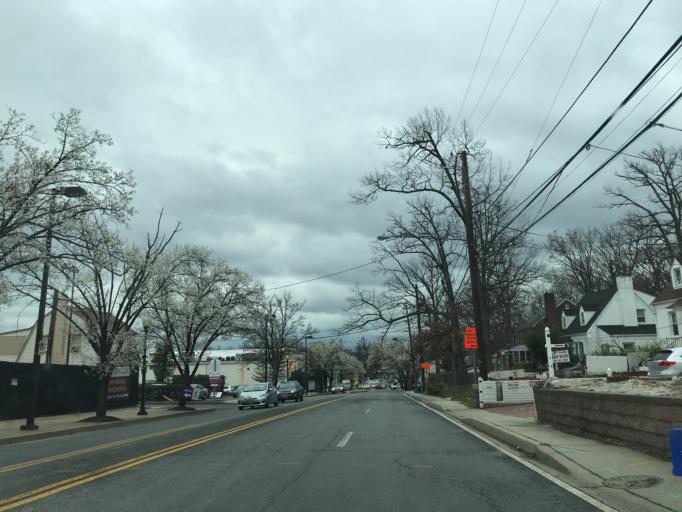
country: US
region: Maryland
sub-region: Montgomery County
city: Four Corners
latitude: 39.0006
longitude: -77.0042
